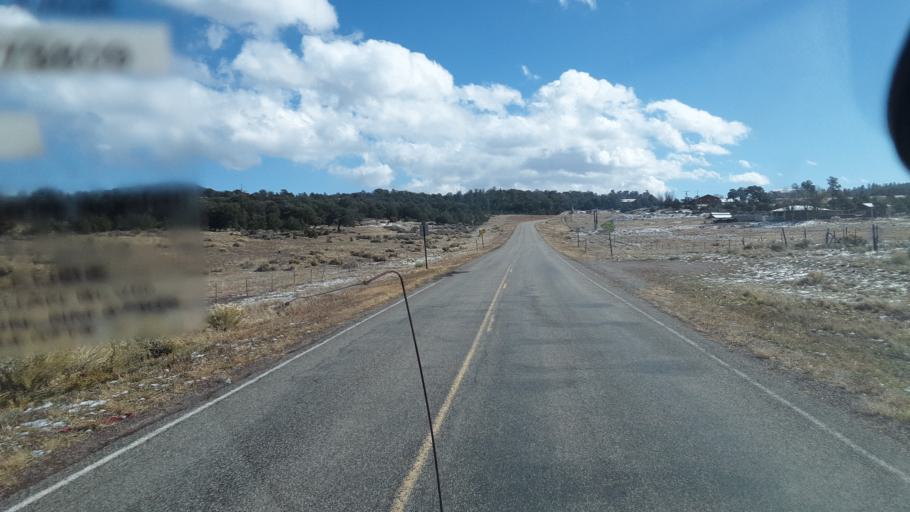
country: US
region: New Mexico
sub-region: Rio Arriba County
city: Santa Teresa
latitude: 36.2326
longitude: -106.8362
